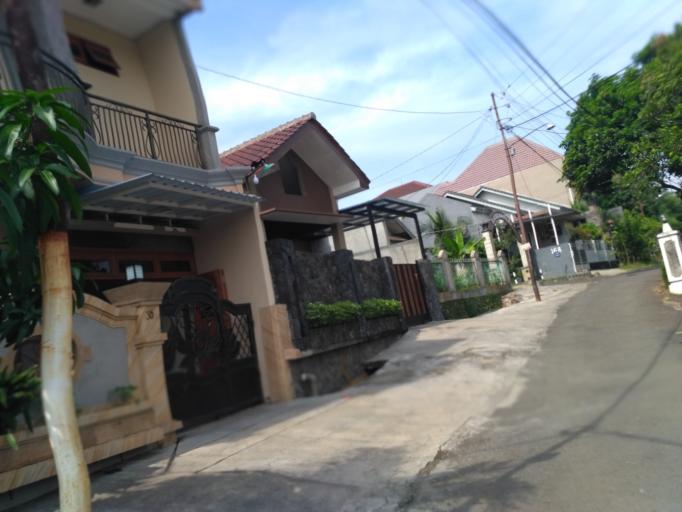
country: ID
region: Central Java
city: Semarang
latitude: -7.0335
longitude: 110.4323
